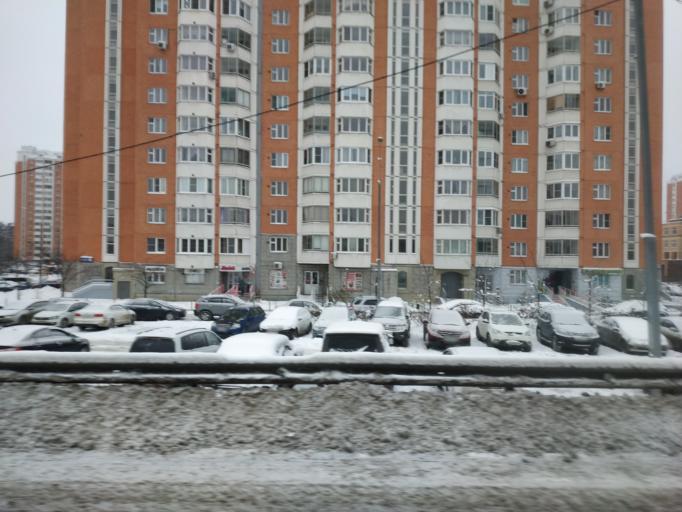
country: RU
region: Moscow
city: Vostochnyy
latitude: 55.8231
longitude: 37.8770
